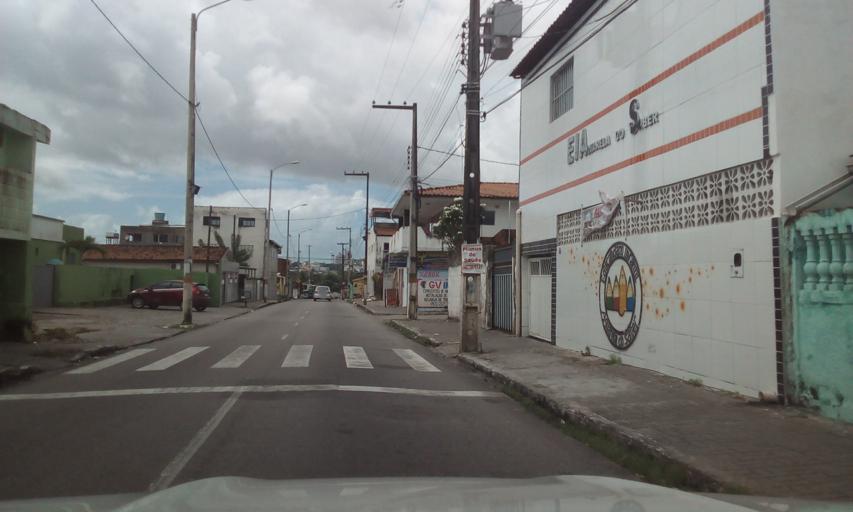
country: BR
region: Paraiba
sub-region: Bayeux
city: Bayeux
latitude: -7.1223
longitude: -34.9064
